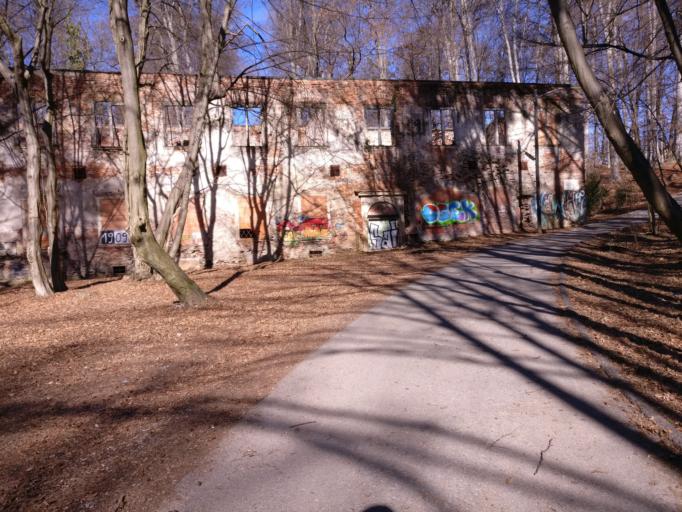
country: AT
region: Styria
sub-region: Graz Stadt
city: Graz
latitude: 47.0853
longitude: 15.4503
